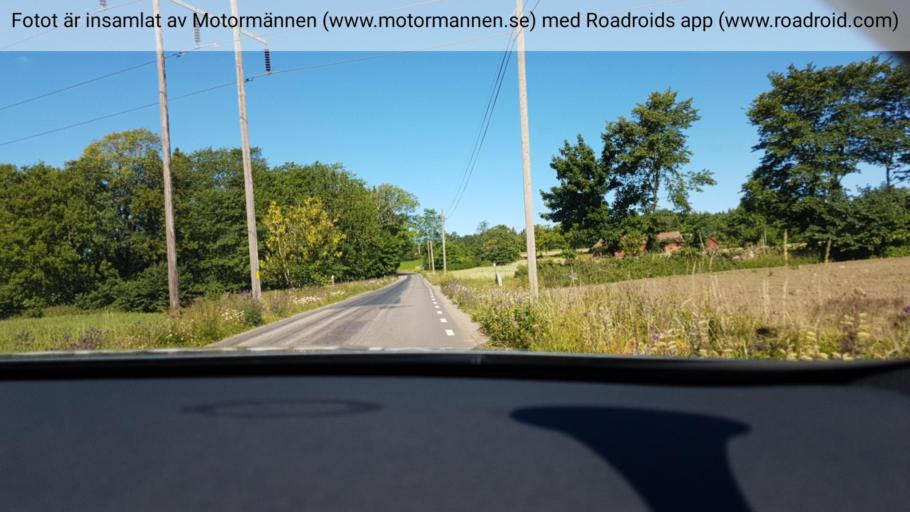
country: SE
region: Vaestra Goetaland
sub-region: Falkopings Kommun
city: Akarp
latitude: 58.2595
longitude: 13.6580
